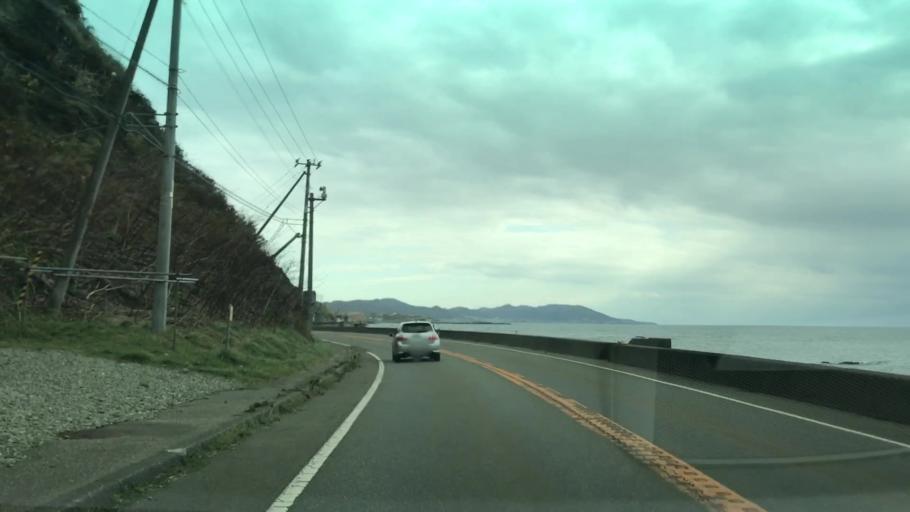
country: JP
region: Hokkaido
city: Shizunai-furukawacho
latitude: 42.0559
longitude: 143.0803
